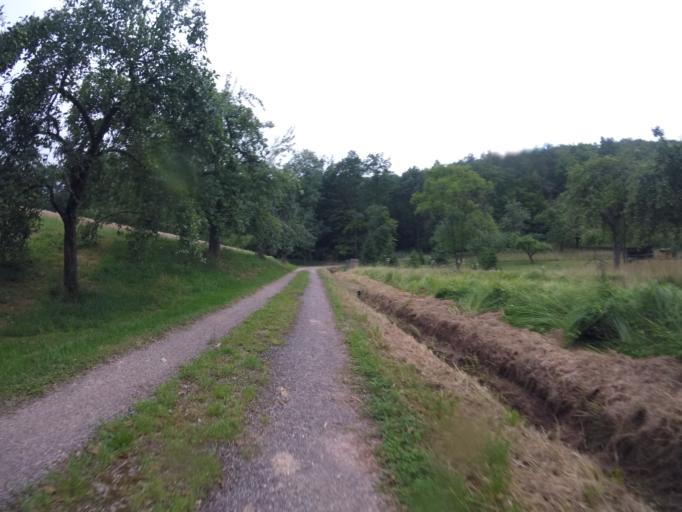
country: DE
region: Baden-Wuerttemberg
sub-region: Regierungsbezirk Stuttgart
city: Oberstenfeld
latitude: 49.0035
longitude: 9.3602
